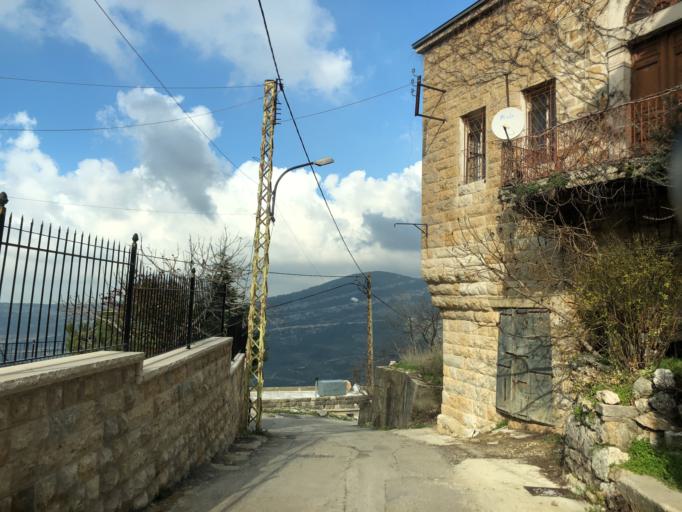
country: LB
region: Liban-Nord
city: Amioun
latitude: 34.2065
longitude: 35.8383
